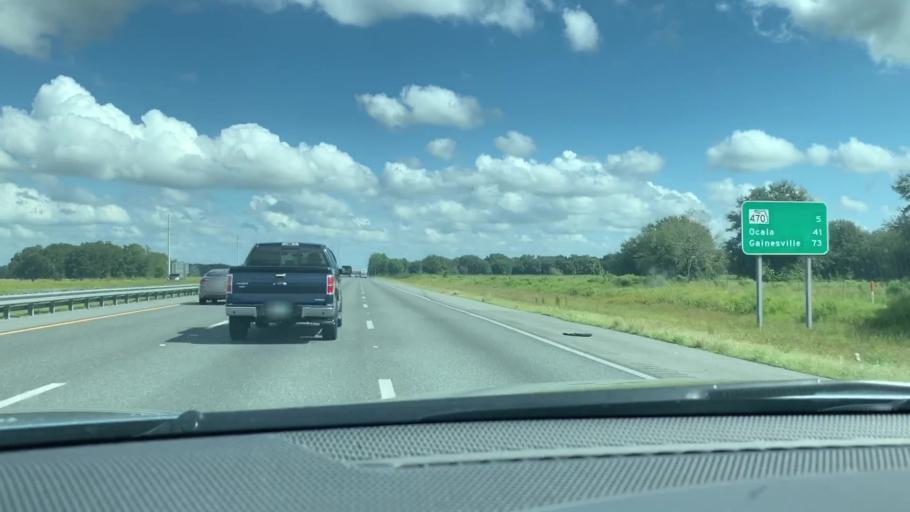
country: US
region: Florida
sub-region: Sumter County
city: Bushnell
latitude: 28.6835
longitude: -82.1356
